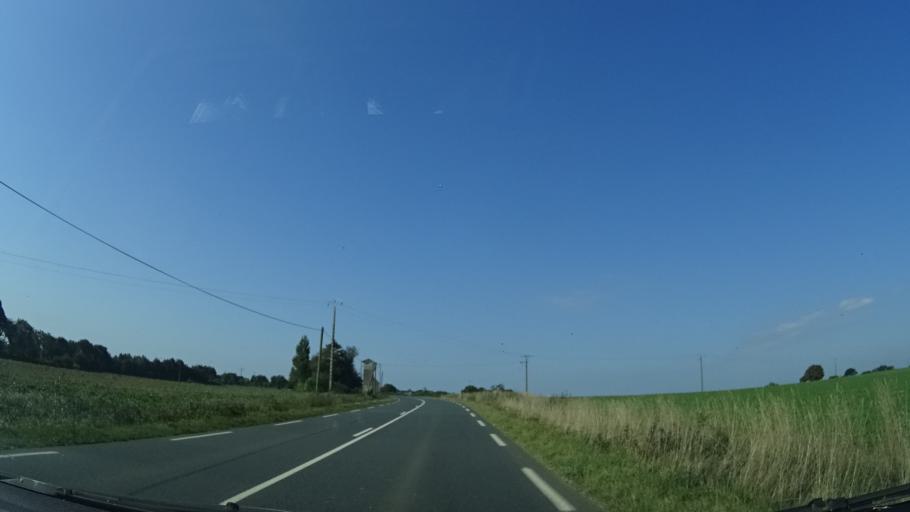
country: FR
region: Brittany
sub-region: Departement du Finistere
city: Cast
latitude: 48.1402
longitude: -4.1730
